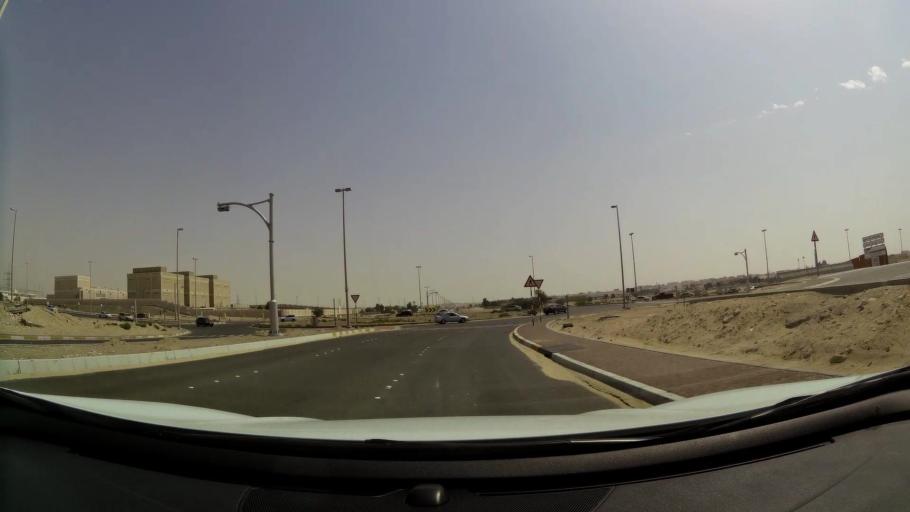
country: AE
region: Abu Dhabi
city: Abu Dhabi
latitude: 24.2927
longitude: 54.6575
